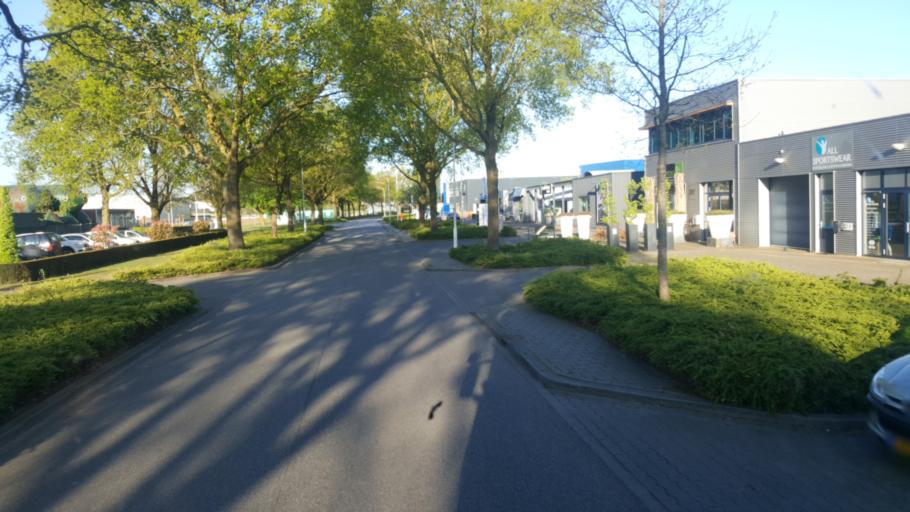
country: NL
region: Gelderland
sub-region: Gemeente Doetinchem
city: Doetinchem
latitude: 51.9548
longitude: 6.2950
